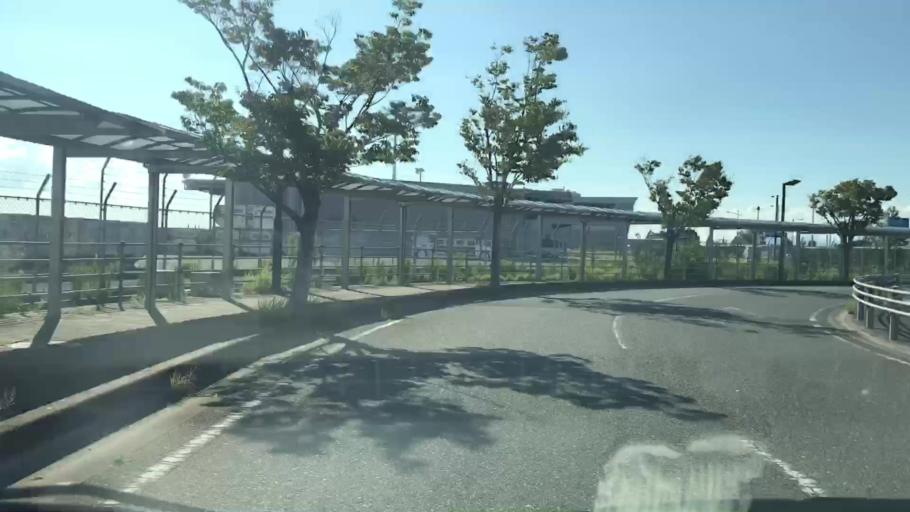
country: JP
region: Saga Prefecture
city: Okawa
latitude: 33.1528
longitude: 130.3060
